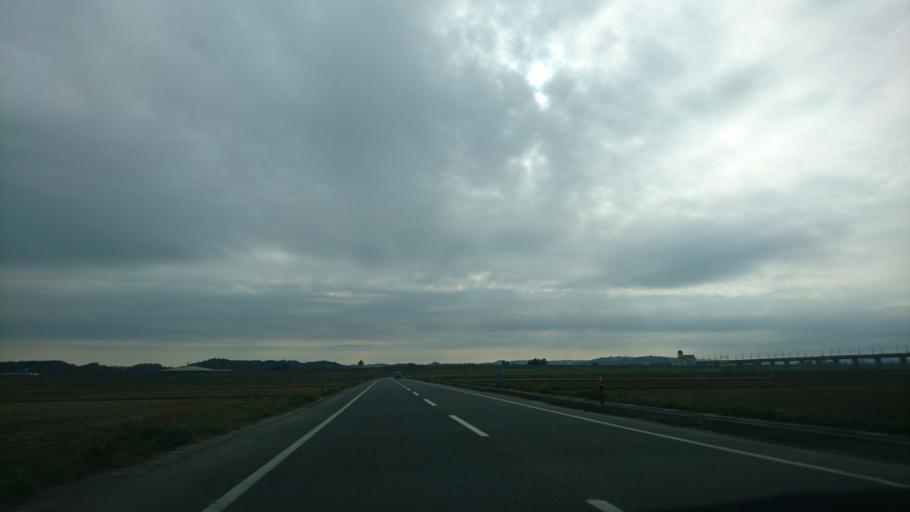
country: JP
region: Iwate
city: Ichinoseki
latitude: 38.9496
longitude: 141.1549
